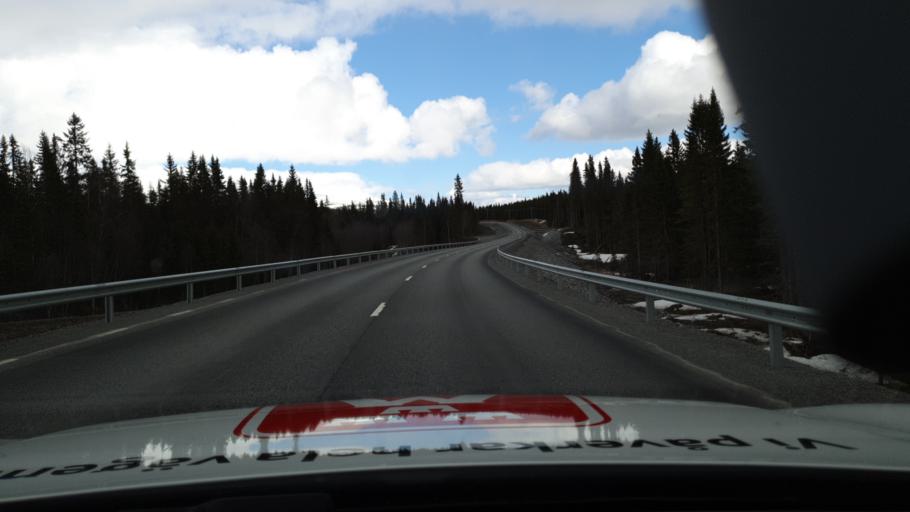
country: SE
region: Jaemtland
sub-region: Are Kommun
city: Are
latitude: 63.3969
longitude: 12.7861
